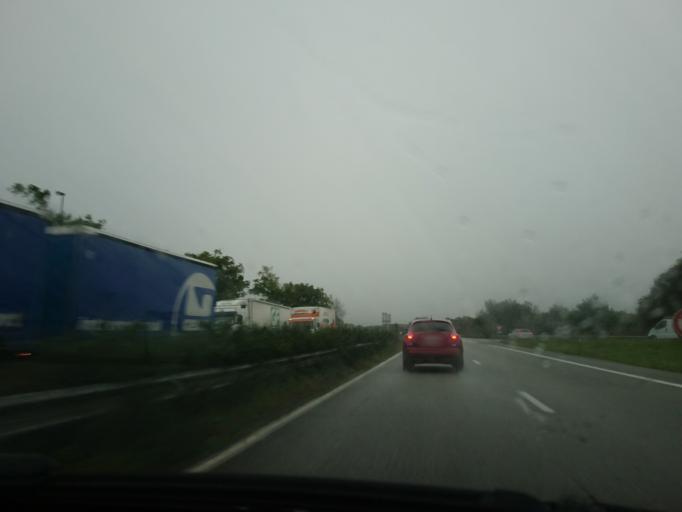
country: FR
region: Brittany
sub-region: Departement du Finistere
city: Ergue-Gaberic
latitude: 47.9766
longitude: -4.0100
